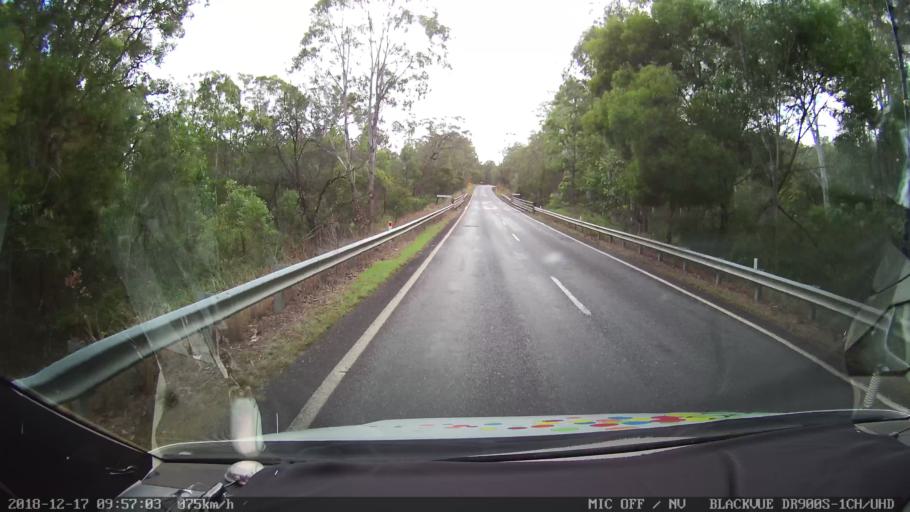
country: AU
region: New South Wales
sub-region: Tenterfield Municipality
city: Carrolls Creek
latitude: -28.9284
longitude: 152.3937
